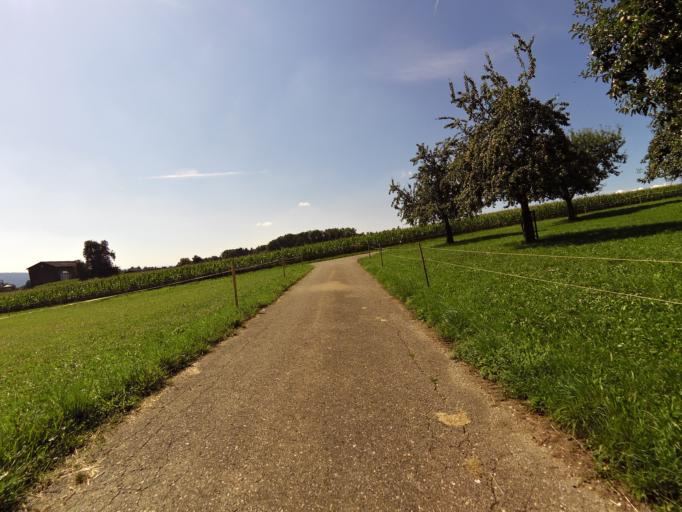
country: CH
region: Thurgau
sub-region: Weinfelden District
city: Maerstetten-Dorf
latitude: 47.6253
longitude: 9.0663
